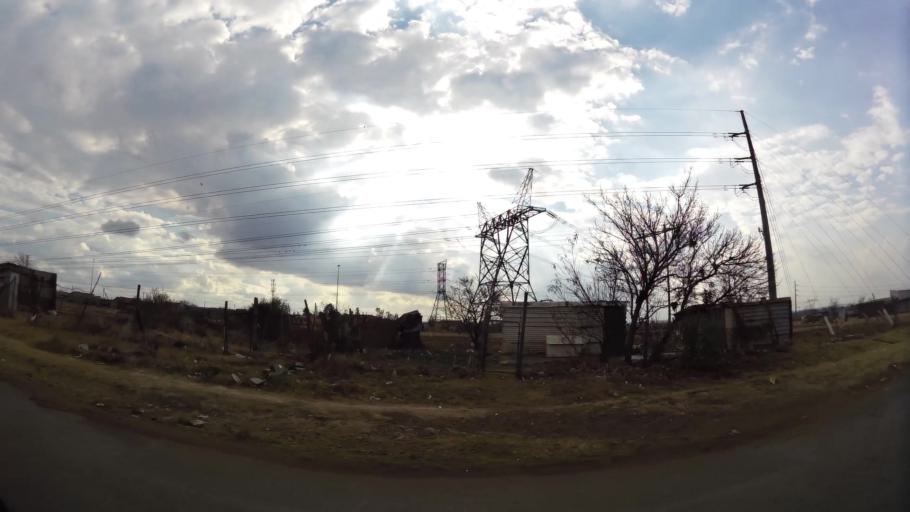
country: ZA
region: Gauteng
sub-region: Sedibeng District Municipality
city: Vereeniging
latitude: -26.6744
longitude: 27.8784
